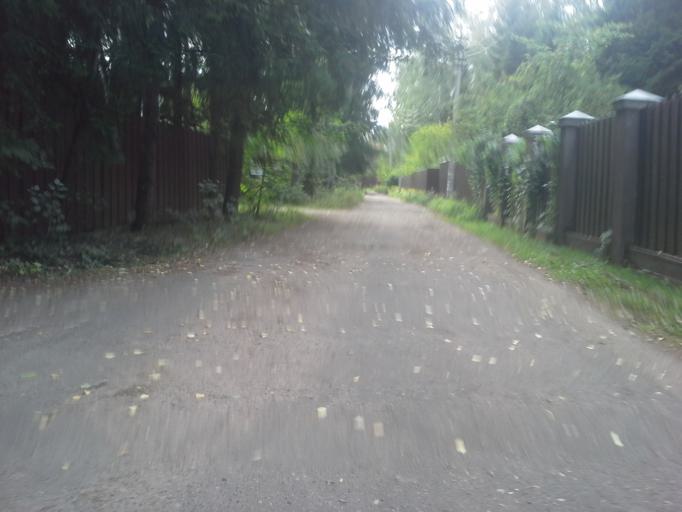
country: RU
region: Moskovskaya
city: Selyatino
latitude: 55.5366
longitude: 37.0203
